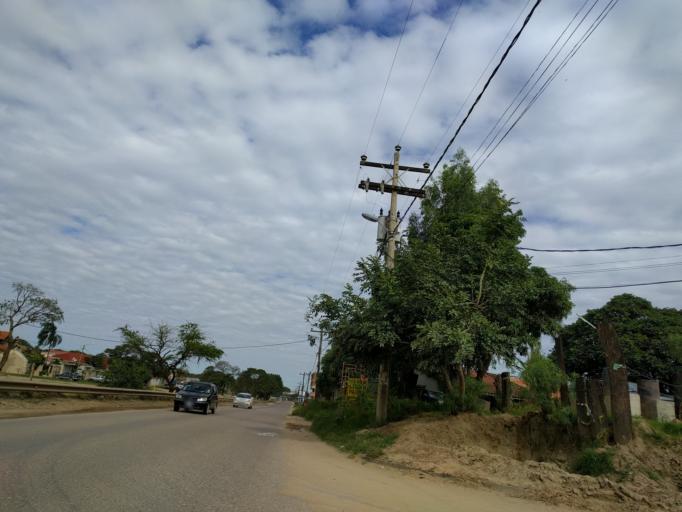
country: BO
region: Santa Cruz
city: Santa Cruz de la Sierra
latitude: -17.8339
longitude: -63.2405
